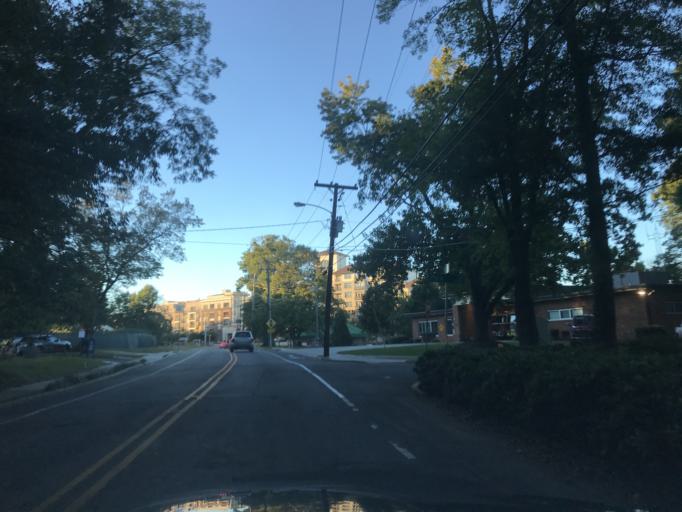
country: US
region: North Carolina
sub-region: Wake County
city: West Raleigh
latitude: 35.7878
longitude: -78.6618
